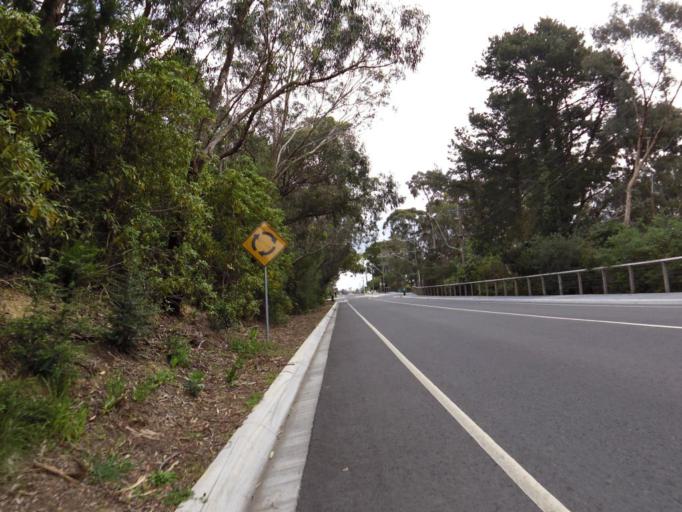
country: AU
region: Victoria
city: Mitcham
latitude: -37.7965
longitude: 145.1961
